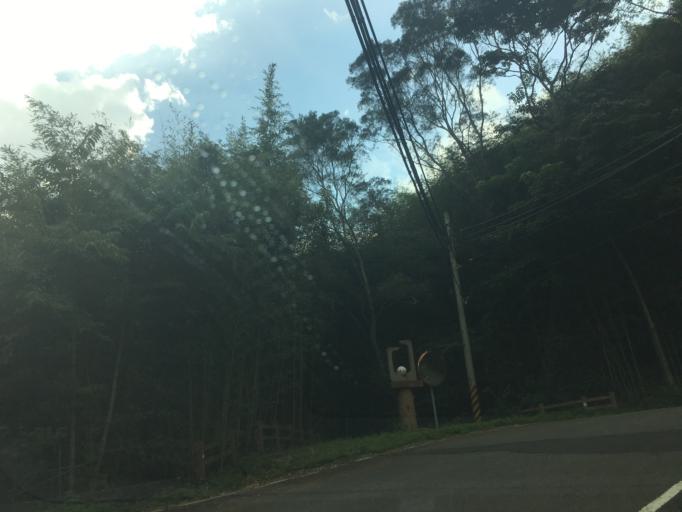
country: TW
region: Taiwan
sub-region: Miaoli
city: Miaoli
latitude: 24.3909
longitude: 120.9750
